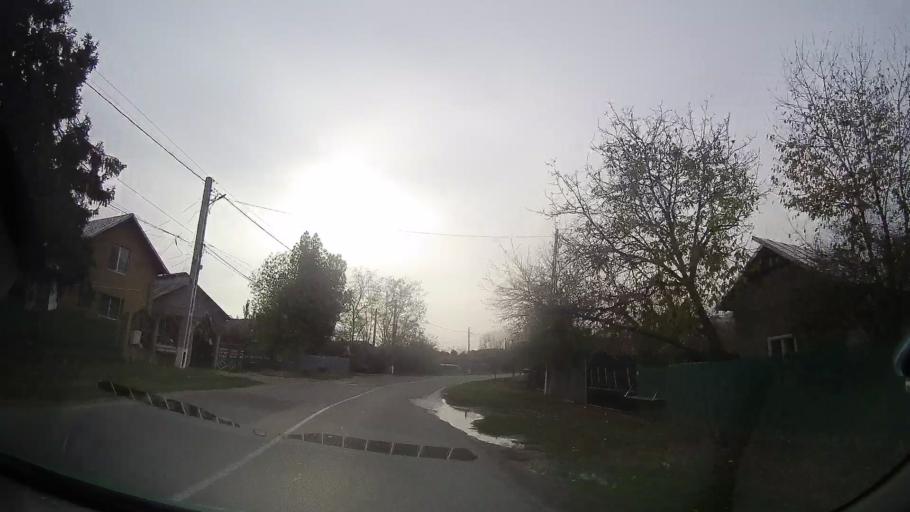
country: RO
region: Prahova
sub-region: Comuna Balta Doamnei
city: Balta Doamnei
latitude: 44.7616
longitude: 26.1419
